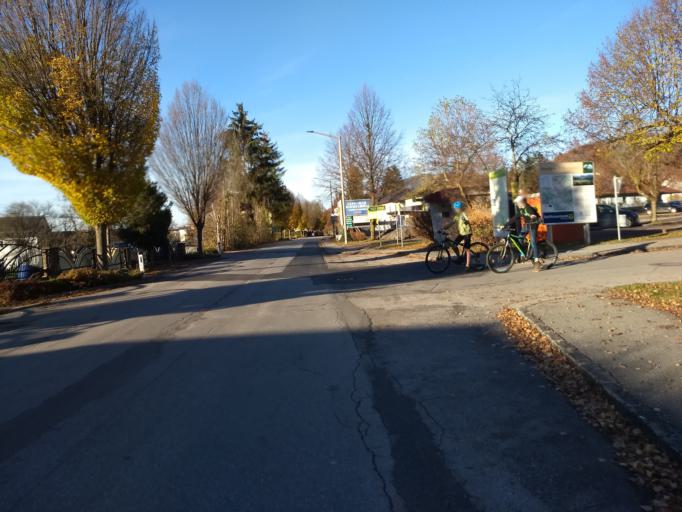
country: AT
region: Upper Austria
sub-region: Politischer Bezirk Kirchdorf an der Krems
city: Micheldorf in Oberoesterreich
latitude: 47.8827
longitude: 14.1329
